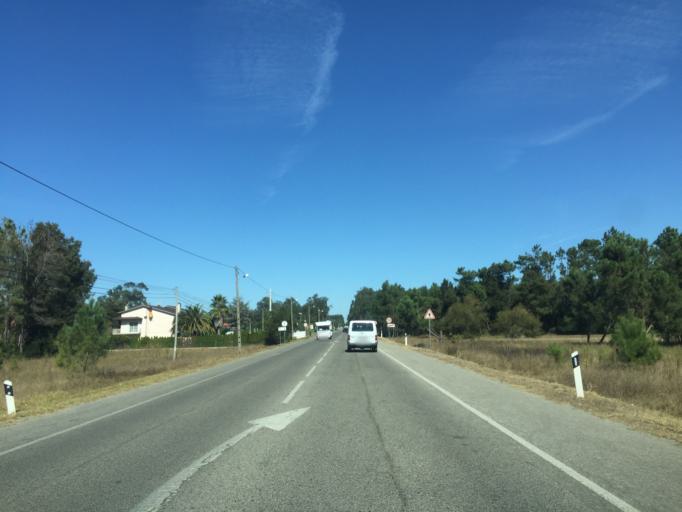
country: PT
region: Coimbra
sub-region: Figueira da Foz
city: Alhadas
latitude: 40.2848
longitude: -8.7691
